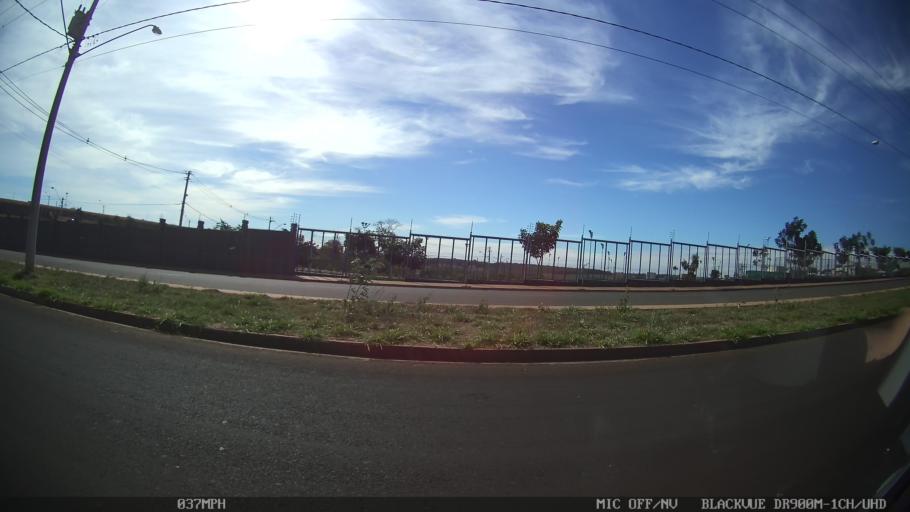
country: BR
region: Sao Paulo
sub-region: Sao Jose Do Rio Preto
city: Sao Jose do Rio Preto
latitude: -20.8049
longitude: -49.3234
